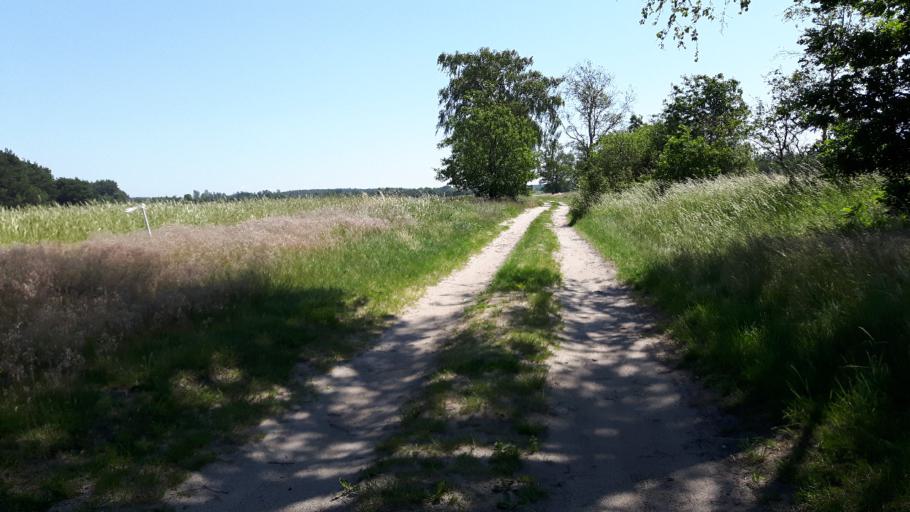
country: PL
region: Pomeranian Voivodeship
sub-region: Powiat slupski
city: Smoldzino
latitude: 54.6701
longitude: 17.1975
